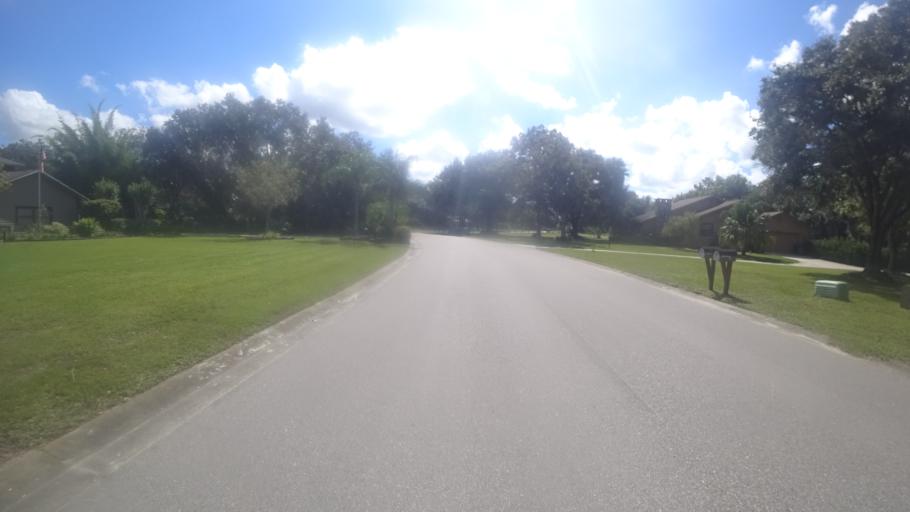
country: US
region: Florida
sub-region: Manatee County
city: Ellenton
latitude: 27.4924
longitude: -82.4061
